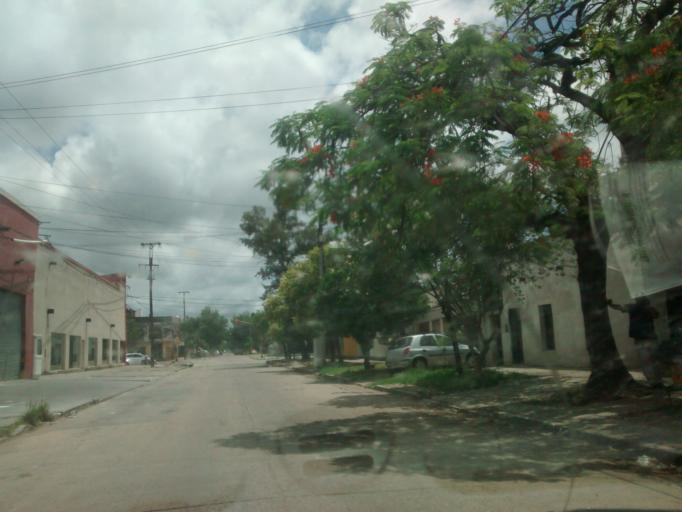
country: AR
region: Chaco
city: Resistencia
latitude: -27.4421
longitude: -58.9980
